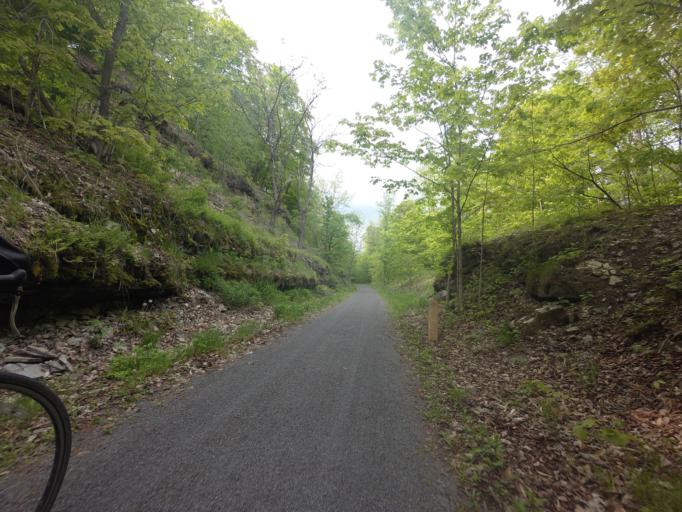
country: CA
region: Ontario
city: Kingston
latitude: 44.3956
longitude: -76.6406
